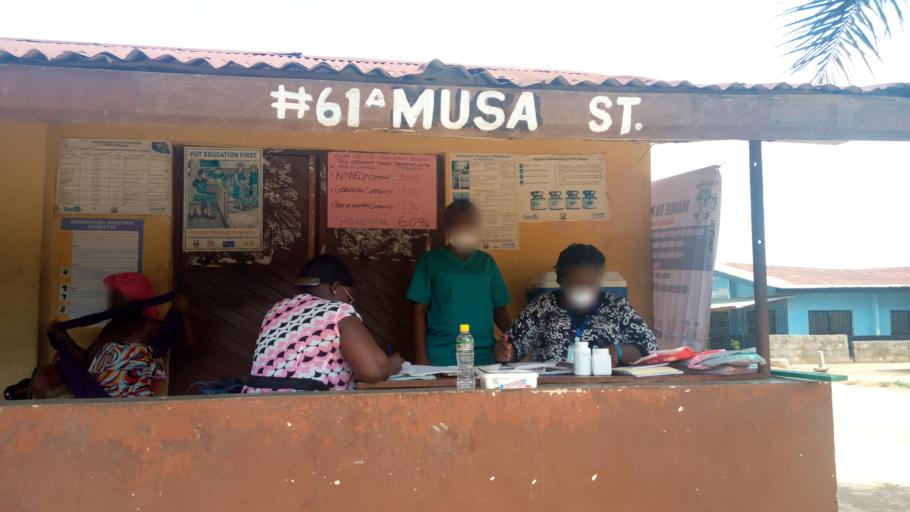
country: SL
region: Southern Province
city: Bo
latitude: 7.9463
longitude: -11.7360
